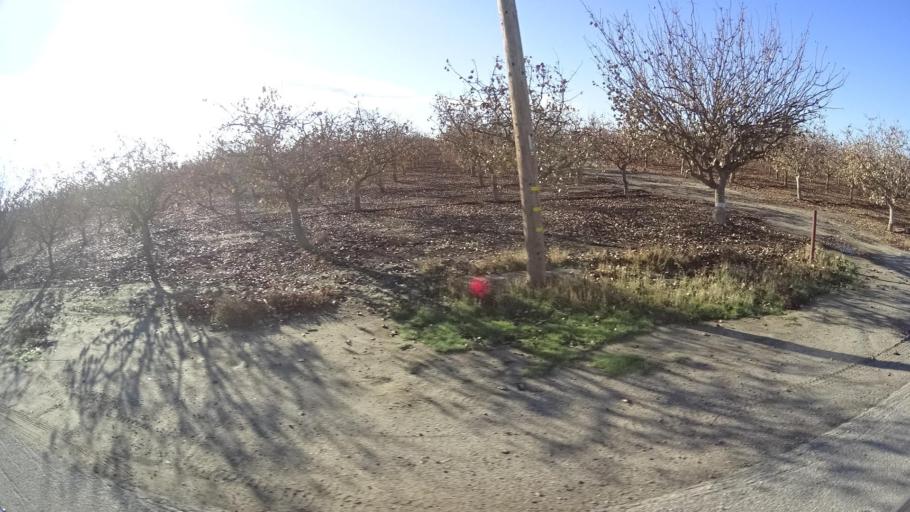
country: US
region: California
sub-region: Kern County
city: Delano
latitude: 35.7757
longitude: -119.3346
